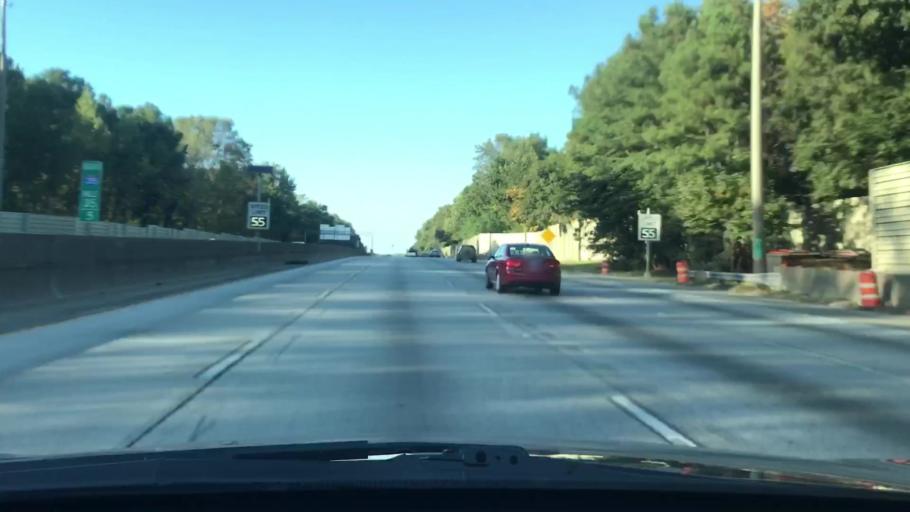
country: US
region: Georgia
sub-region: DeKalb County
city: Tucker
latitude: 33.8590
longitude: -84.2473
